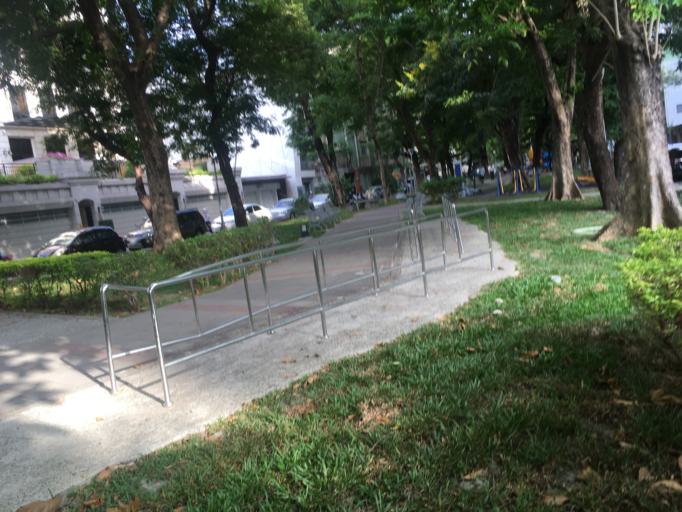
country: TW
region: Kaohsiung
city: Kaohsiung
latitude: 22.6229
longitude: 120.3223
